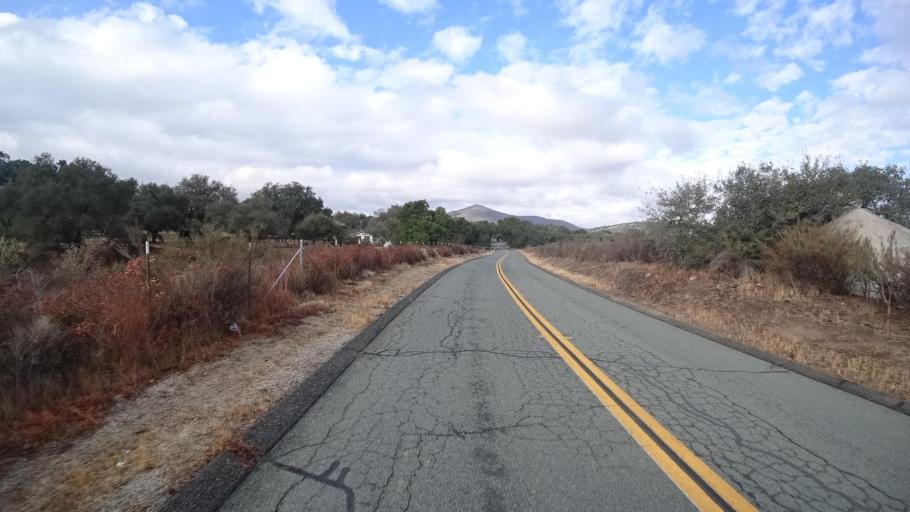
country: MX
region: Baja California
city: Tecate
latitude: 32.6265
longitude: -116.5958
